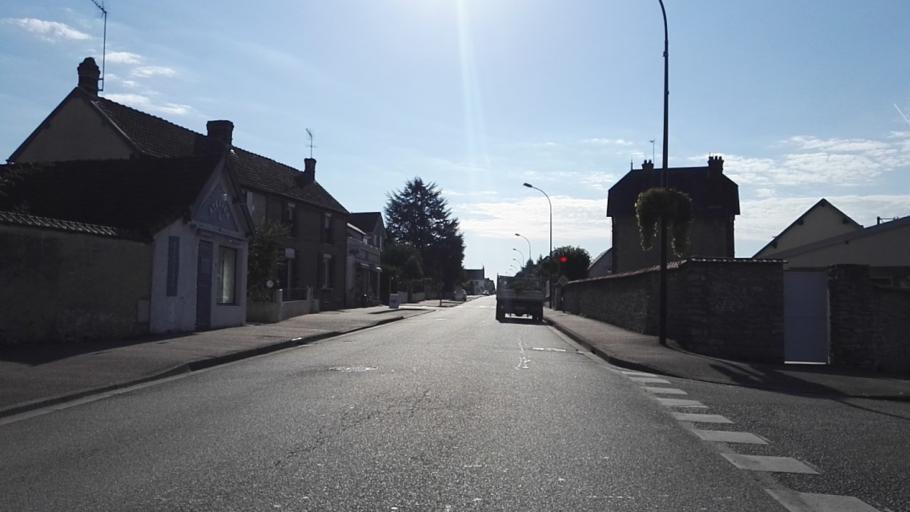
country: FR
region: Haute-Normandie
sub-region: Departement de l'Eure
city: Pacy-sur-Eure
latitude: 49.0190
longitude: 1.3807
